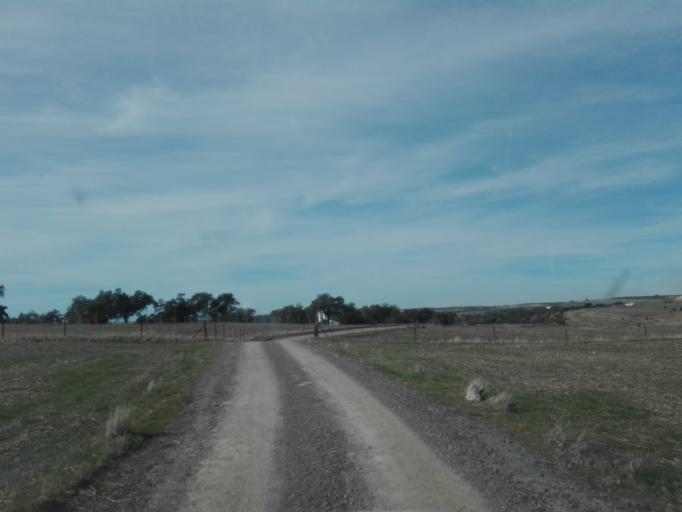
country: ES
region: Extremadura
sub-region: Provincia de Badajoz
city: Valverde de Llerena
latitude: 38.2362
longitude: -5.7500
